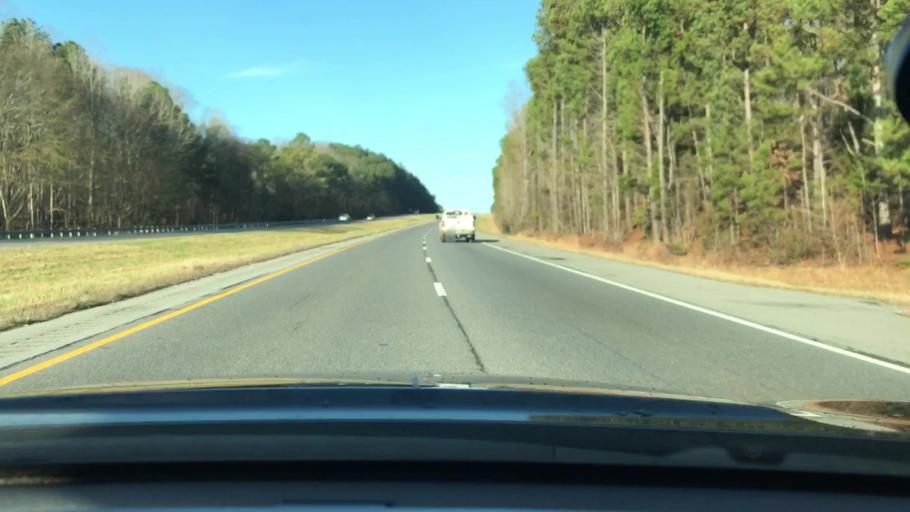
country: US
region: Alabama
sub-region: Shelby County
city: Harpersville
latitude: 33.3524
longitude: -86.4777
